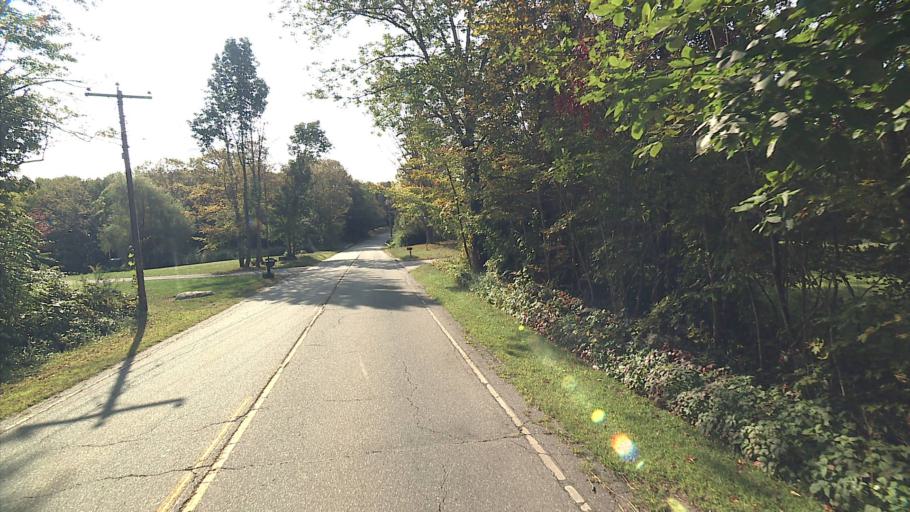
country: US
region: Connecticut
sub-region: Windham County
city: Willimantic
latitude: 41.6582
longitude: -72.2480
